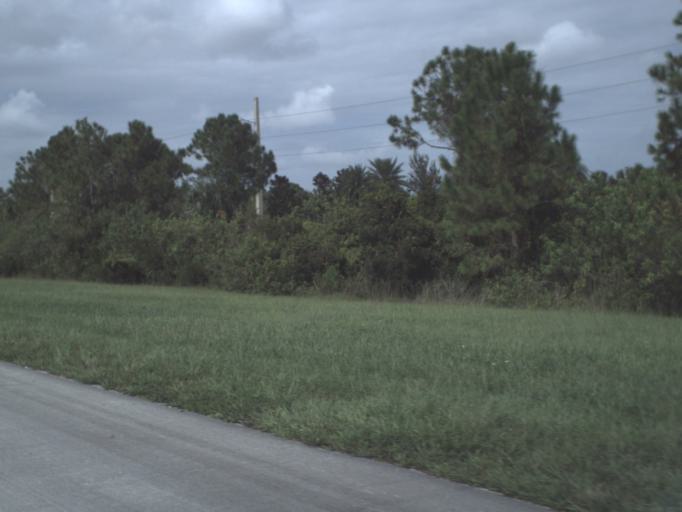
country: US
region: Florida
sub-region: Martin County
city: Palm City
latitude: 27.1351
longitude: -80.2867
